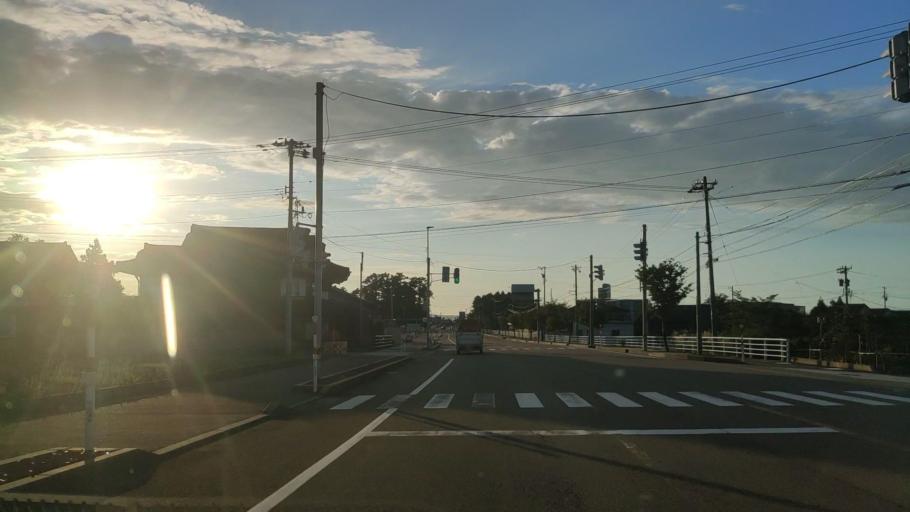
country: JP
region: Toyama
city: Nanto-shi
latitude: 36.5719
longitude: 136.9860
